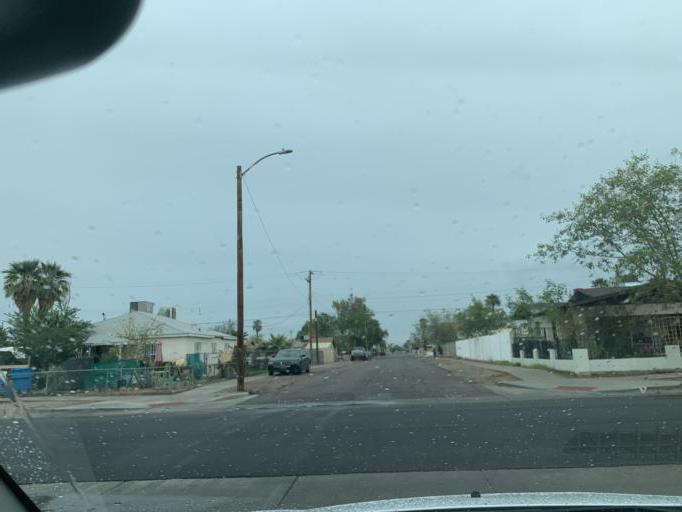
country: US
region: Arizona
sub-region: Maricopa County
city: Phoenix
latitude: 33.4548
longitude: -112.0544
